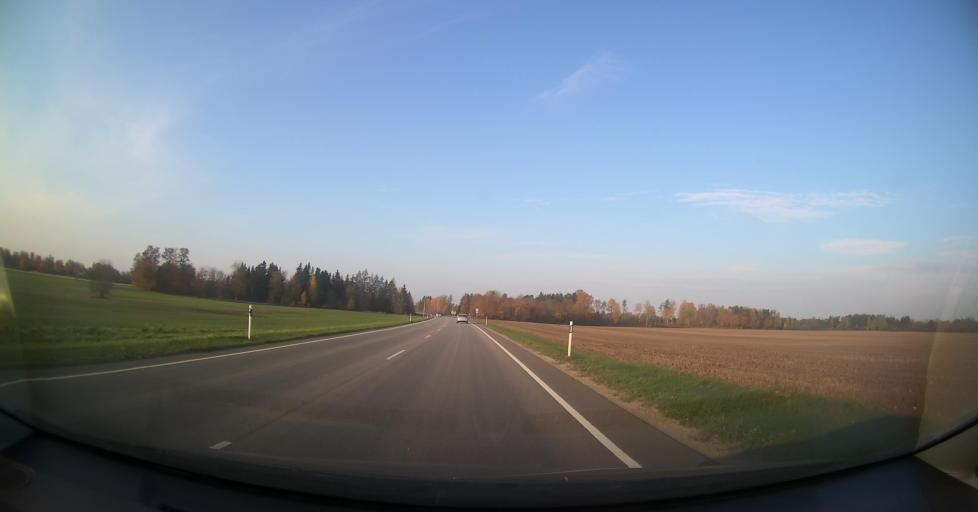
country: EE
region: Laeaene
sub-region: Ridala Parish
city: Uuemoisa
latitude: 58.9612
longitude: 23.6822
